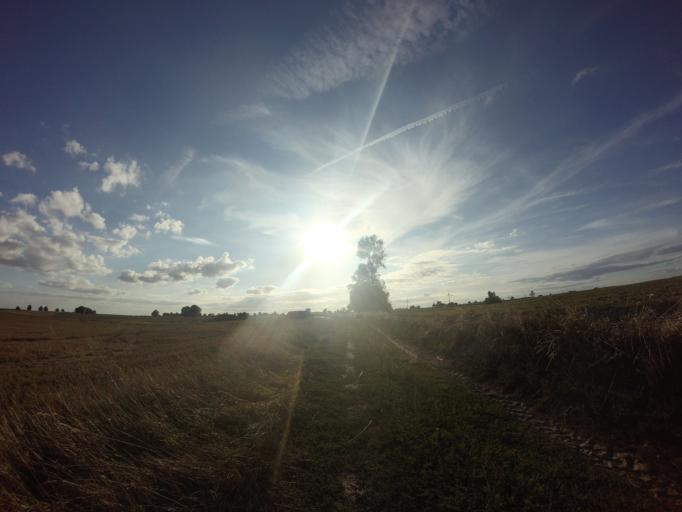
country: PL
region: West Pomeranian Voivodeship
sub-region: Powiat choszczenski
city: Krzecin
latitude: 53.1065
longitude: 15.4711
